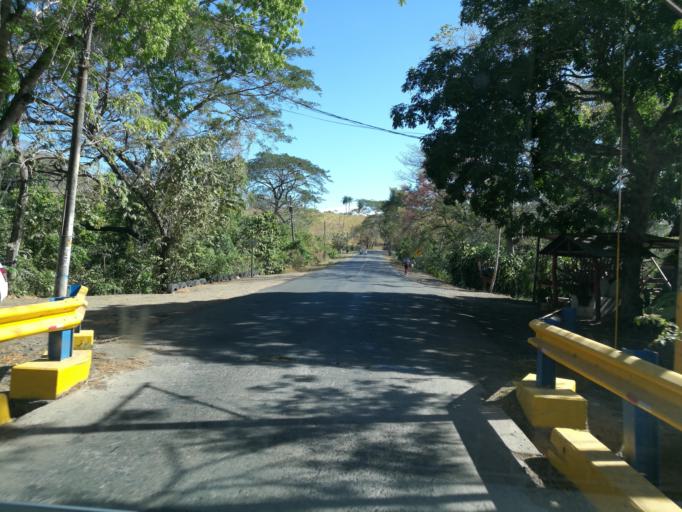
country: CR
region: Puntarenas
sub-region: Canton Central de Puntarenas
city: Puntarenas
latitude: 10.1092
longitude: -84.9195
